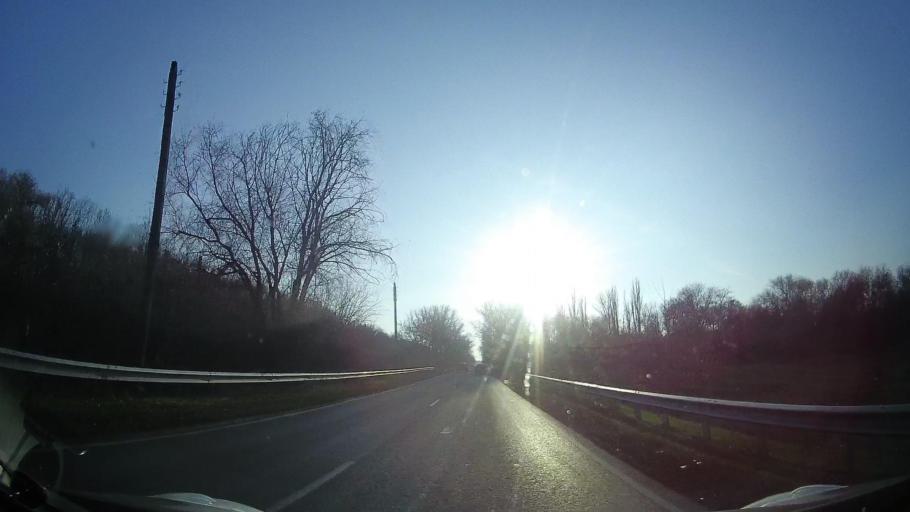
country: RU
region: Rostov
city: Ol'ginskaya
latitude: 47.1727
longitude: 39.9473
